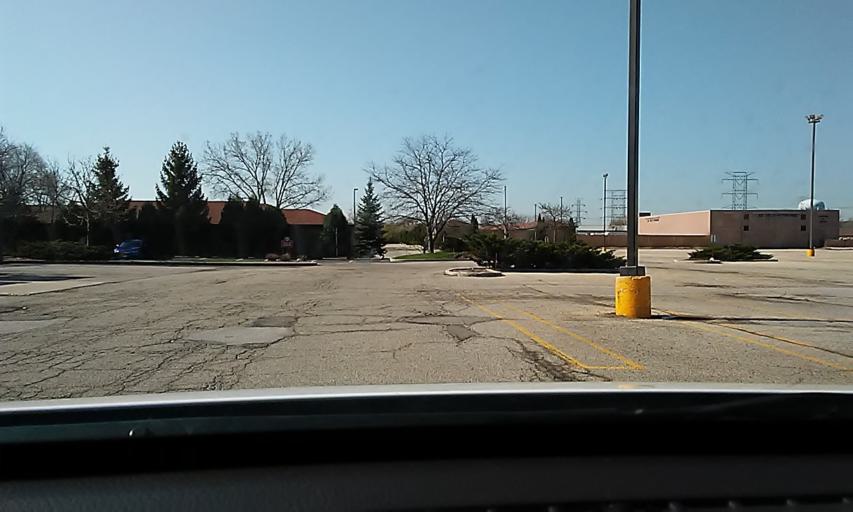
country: US
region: Wisconsin
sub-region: Waukesha County
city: Elm Grove
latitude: 43.0159
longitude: -88.0497
